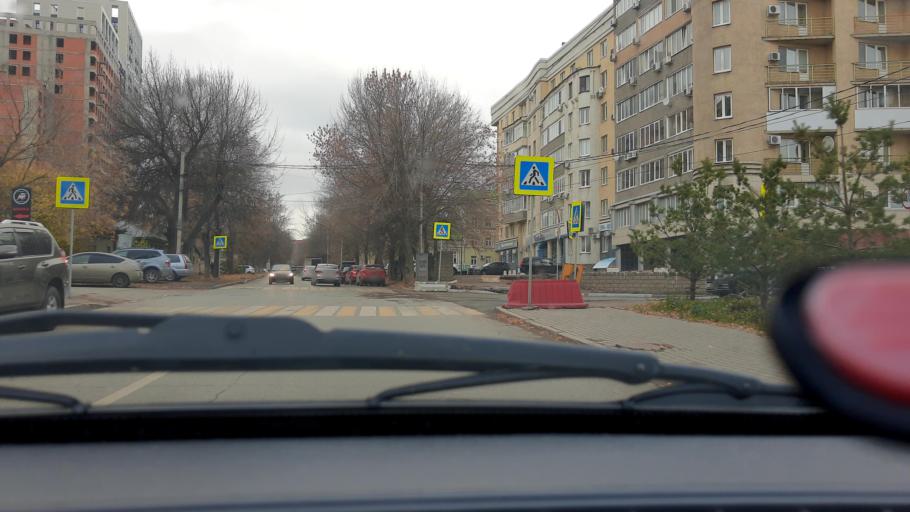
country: RU
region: Bashkortostan
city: Ufa
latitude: 54.7208
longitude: 55.9614
